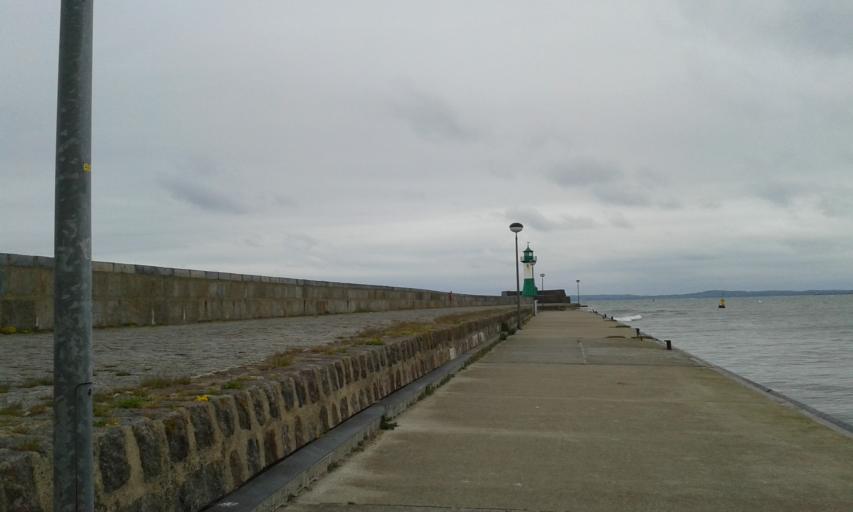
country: DE
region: Mecklenburg-Vorpommern
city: Sassnitz
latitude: 54.5077
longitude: 13.6384
